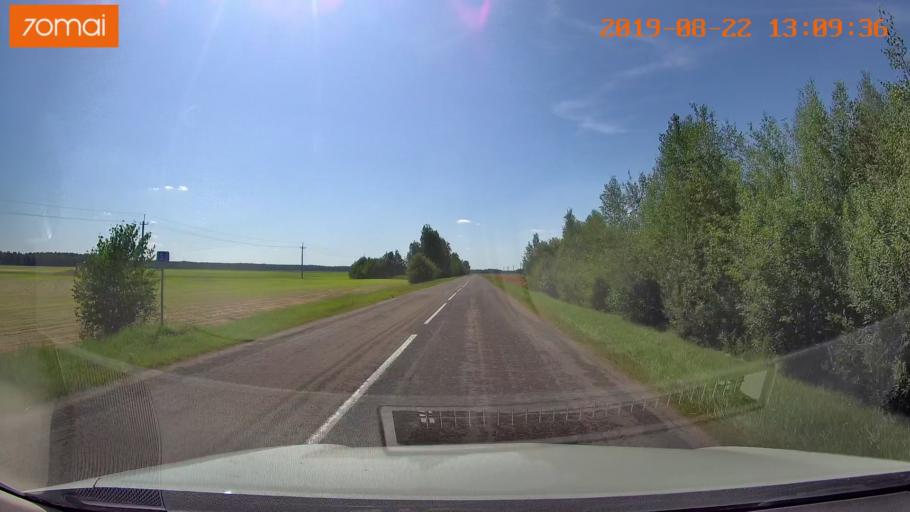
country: BY
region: Minsk
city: Prawdzinski
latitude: 53.3082
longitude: 27.8505
